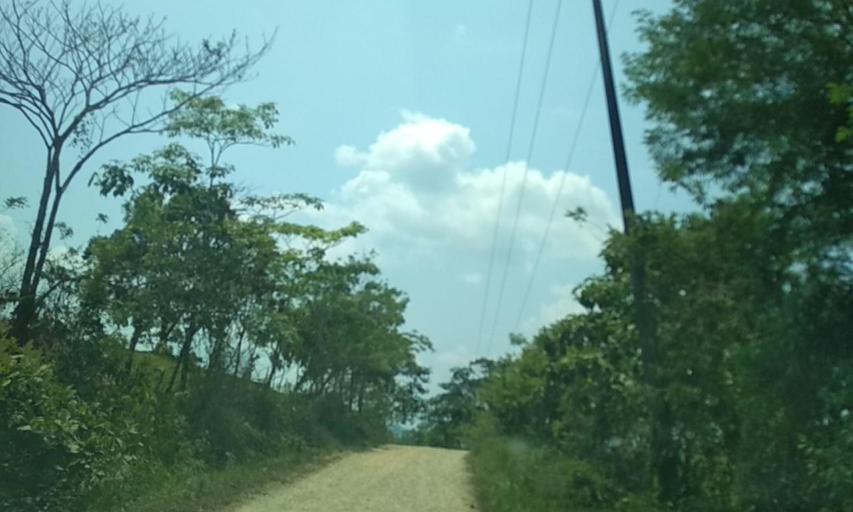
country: MX
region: Chiapas
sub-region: Tecpatan
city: Raudales Malpaso
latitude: 17.3442
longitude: -93.9596
